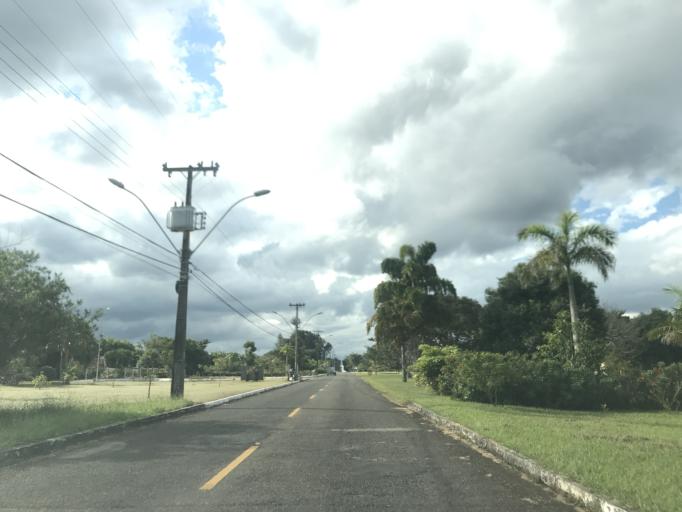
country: BR
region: Federal District
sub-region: Brasilia
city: Brasilia
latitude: -15.9137
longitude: -47.9418
